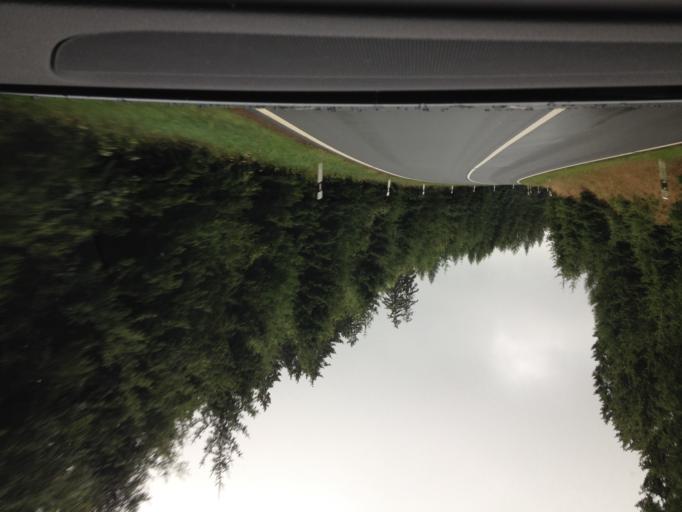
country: DE
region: Hesse
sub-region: Regierungsbezirk Darmstadt
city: Schlangenbad
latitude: 50.1109
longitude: 8.1220
